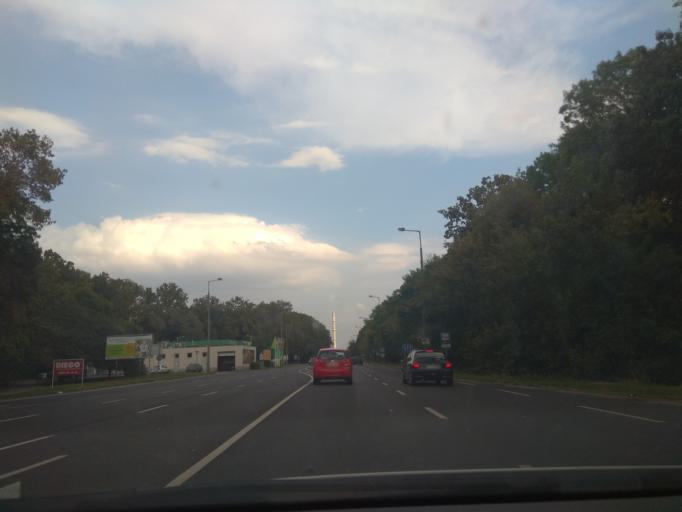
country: HU
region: Borsod-Abauj-Zemplen
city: Sajooeroes
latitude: 47.9262
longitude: 21.0398
